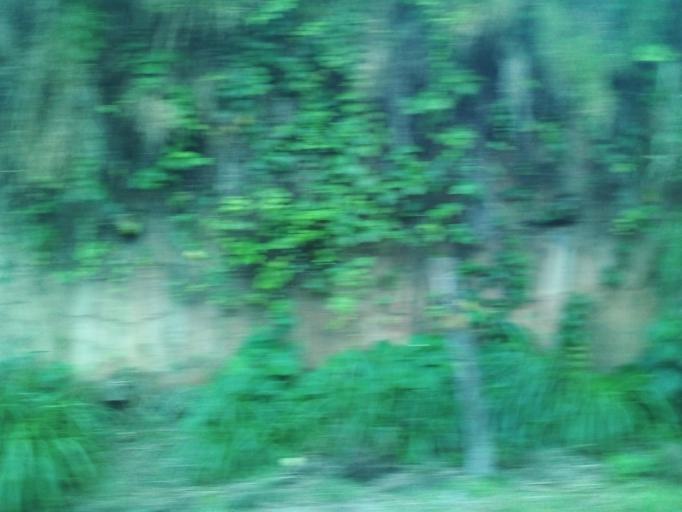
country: BR
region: Minas Gerais
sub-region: Joao Monlevade
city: Joao Monlevade
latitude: -19.8321
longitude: -43.1283
